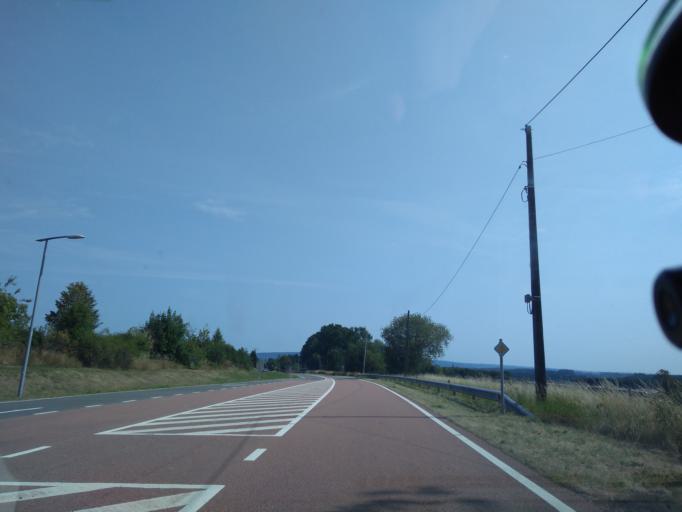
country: BE
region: Wallonia
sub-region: Province du Luxembourg
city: Tenneville
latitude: 50.1470
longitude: 5.5113
